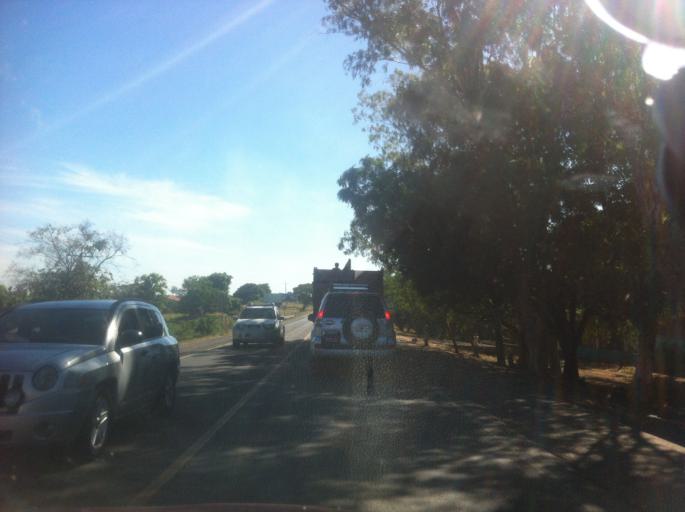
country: NI
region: Managua
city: Tipitapa
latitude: 12.3015
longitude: -86.0556
